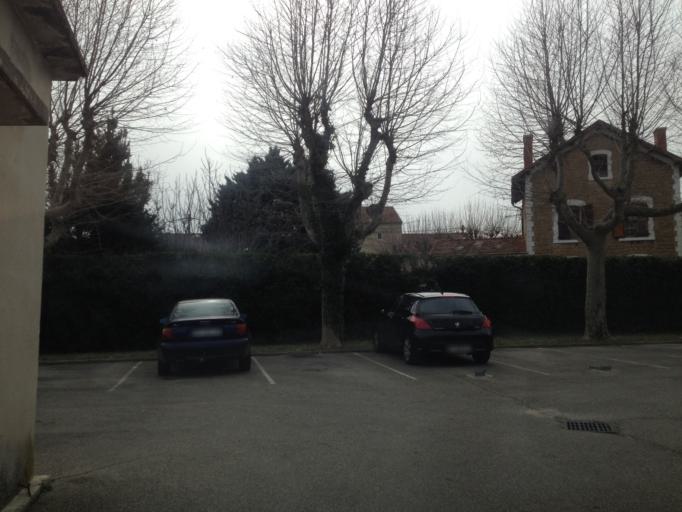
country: FR
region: Provence-Alpes-Cote d'Azur
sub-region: Departement du Vaucluse
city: Orange
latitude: 44.1396
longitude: 4.8179
